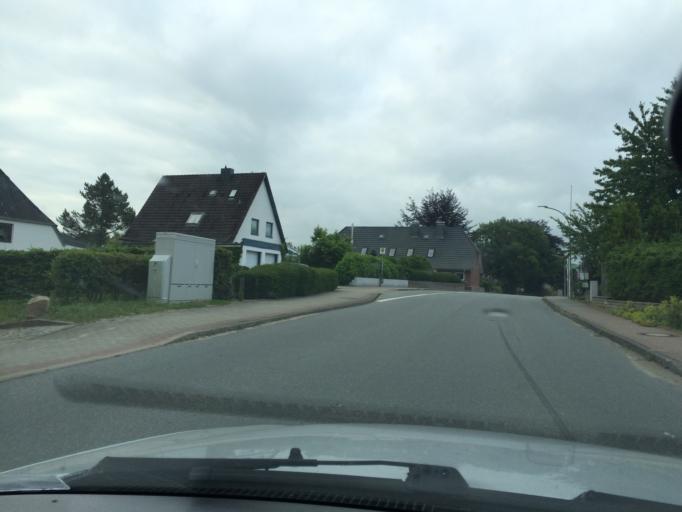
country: DE
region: Schleswig-Holstein
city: Oeversee
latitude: 54.6928
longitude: 9.4265
